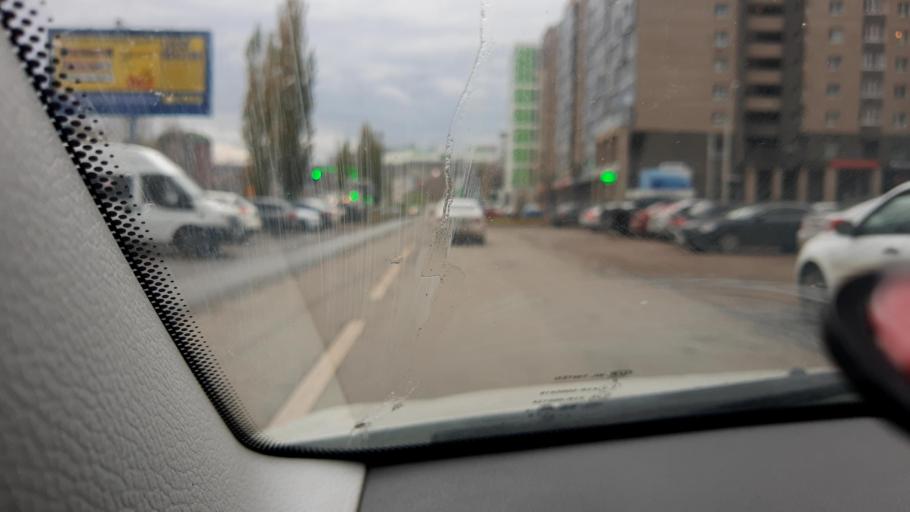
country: RU
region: Bashkortostan
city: Ufa
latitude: 54.7665
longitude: 56.0501
